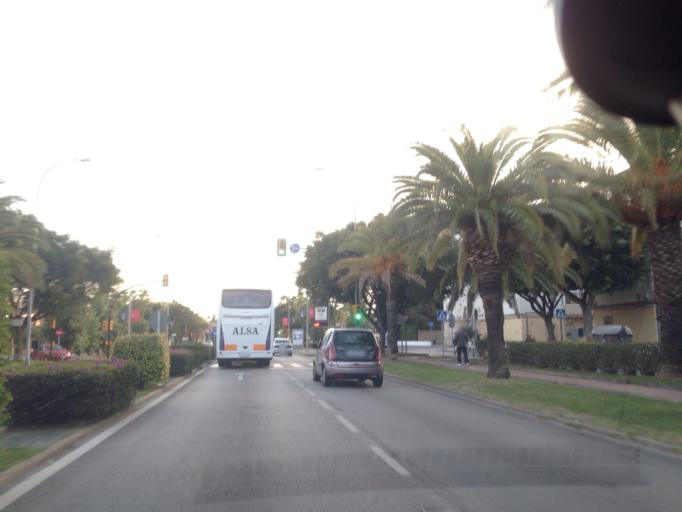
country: ES
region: Andalusia
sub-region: Provincia de Malaga
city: Malaga
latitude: 36.7409
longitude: -4.4234
